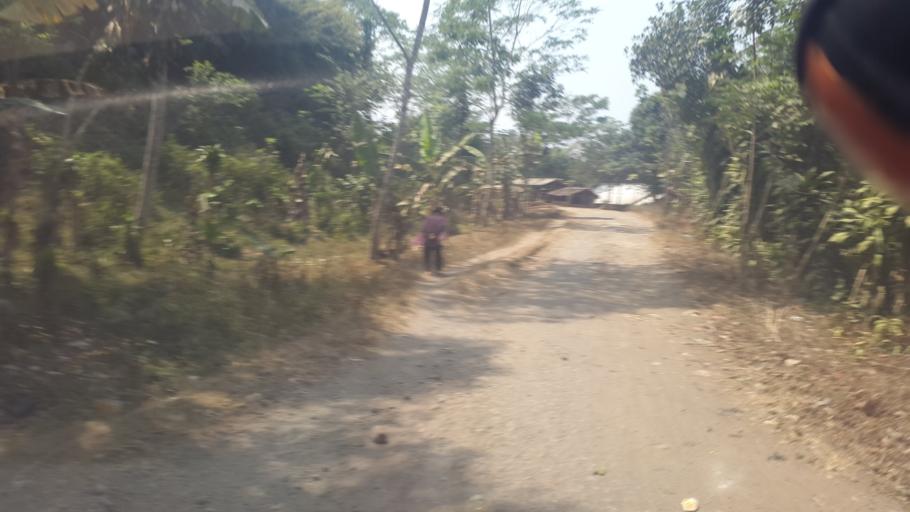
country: ID
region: West Java
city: Ciroyom
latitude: -7.0951
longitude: 106.8255
